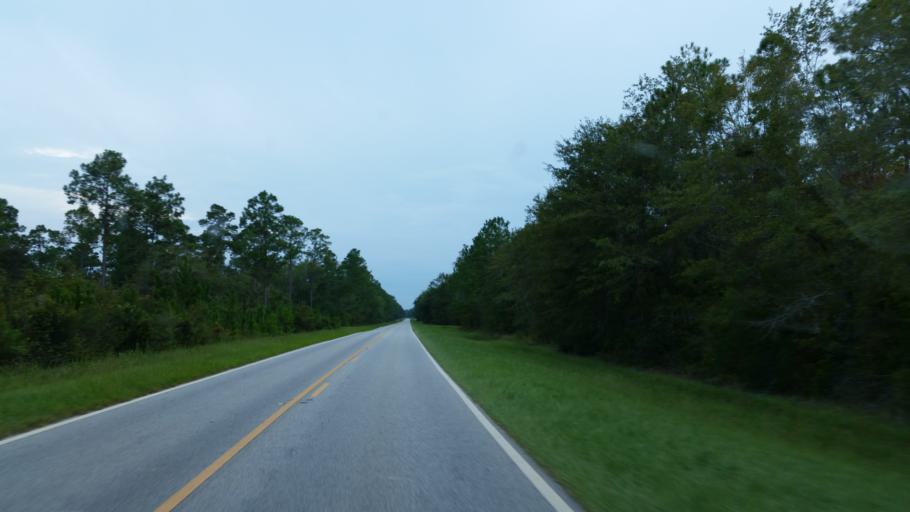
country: US
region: Georgia
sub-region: Lowndes County
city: Valdosta
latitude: 30.7557
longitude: -83.3058
